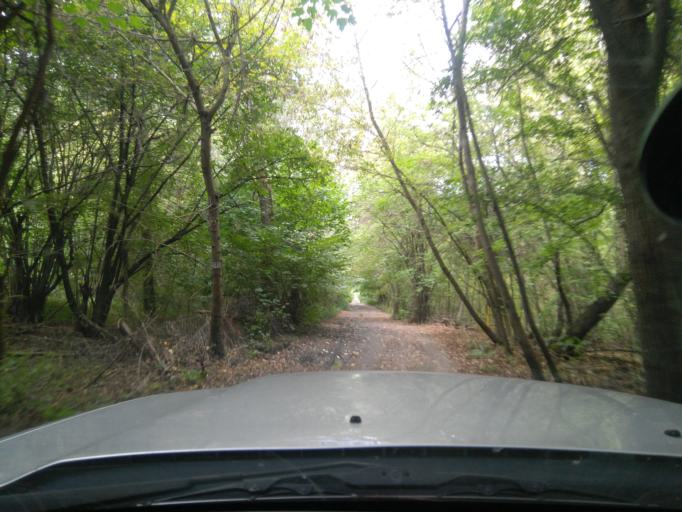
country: HU
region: Bacs-Kiskun
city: Apostag
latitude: 46.8945
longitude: 18.9463
